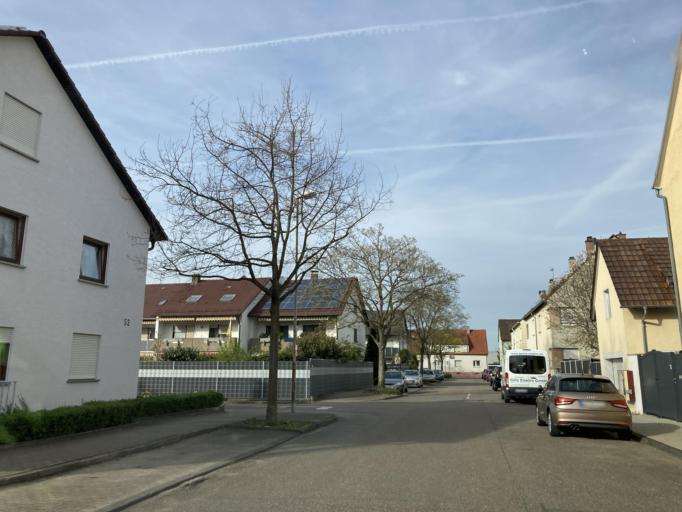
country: DE
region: Baden-Wuerttemberg
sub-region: Karlsruhe Region
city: Weingarten
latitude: 49.0898
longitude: 8.5528
